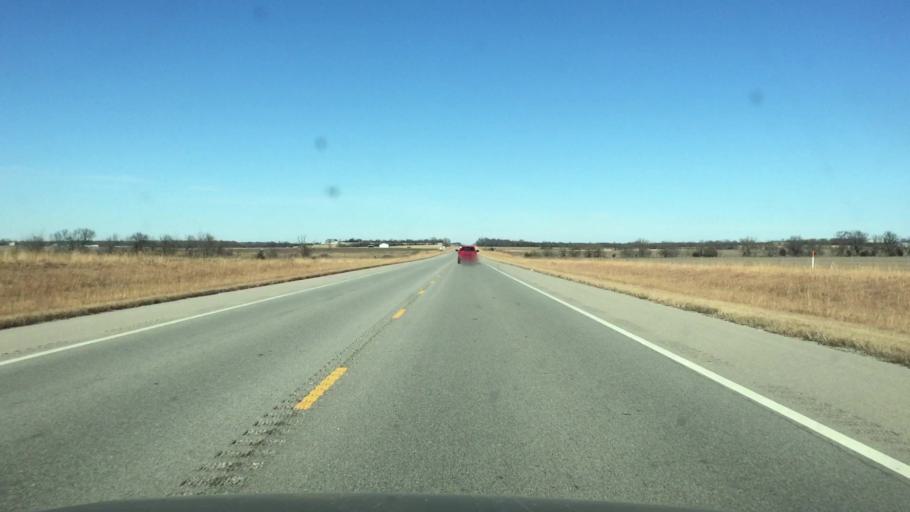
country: US
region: Kansas
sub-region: Allen County
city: Iola
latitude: 37.9548
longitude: -95.3812
